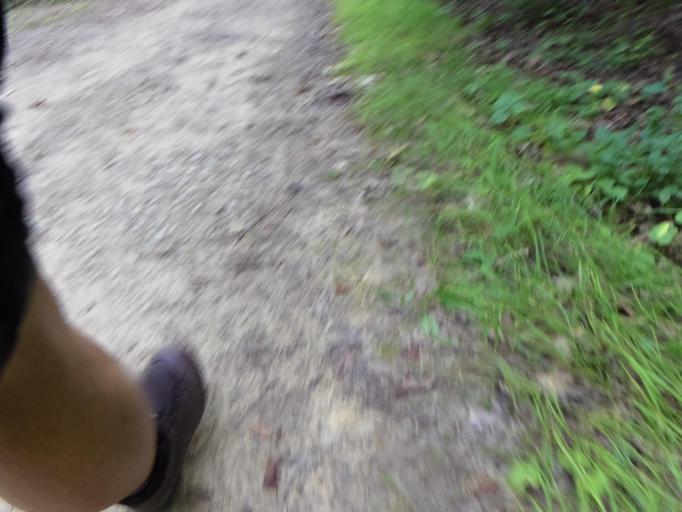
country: US
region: Minnesota
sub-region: Washington County
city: Afton
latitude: 44.8523
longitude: -92.7723
